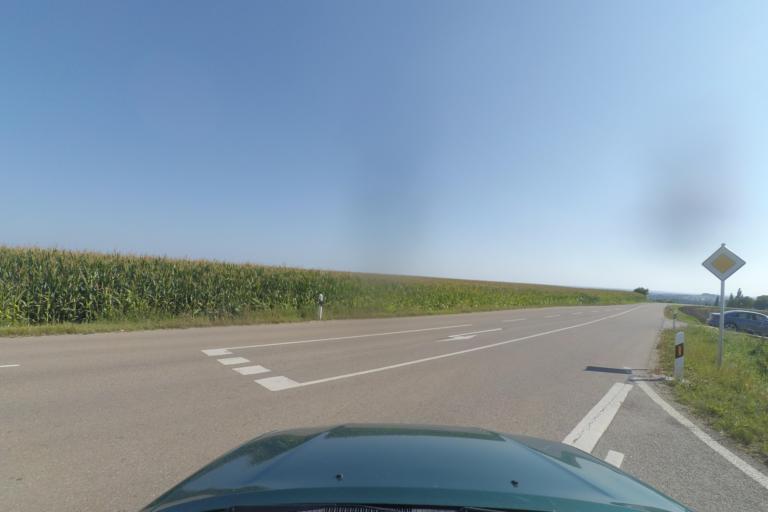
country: DE
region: Bavaria
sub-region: Swabia
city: Donauwoerth
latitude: 48.7380
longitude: 10.7549
